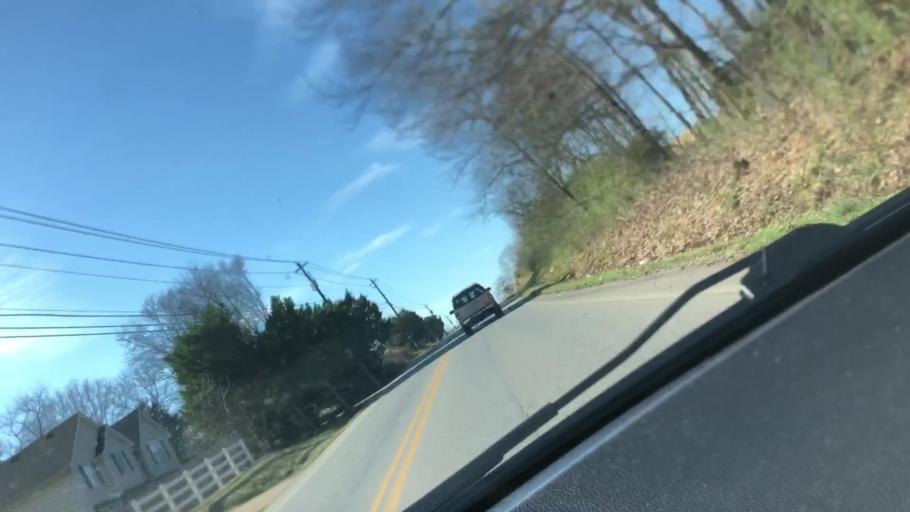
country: US
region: Georgia
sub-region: Bartow County
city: Cartersville
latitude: 34.2224
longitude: -84.8066
